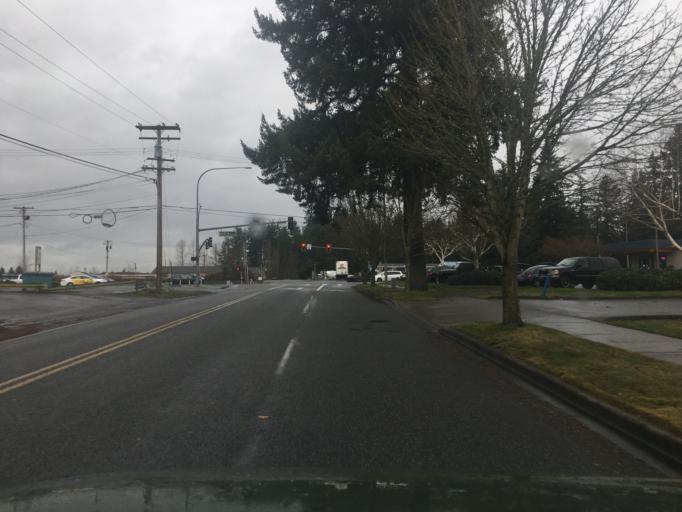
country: US
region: Washington
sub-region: Thurston County
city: Tanglewilde-Thompson Place
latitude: 47.0507
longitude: -122.7913
